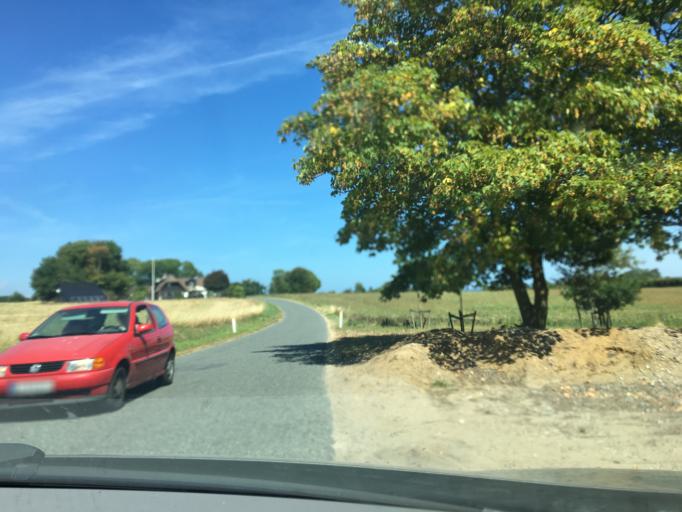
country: DK
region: South Denmark
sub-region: Middelfart Kommune
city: Norre Aby
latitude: 55.5177
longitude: 9.8430
